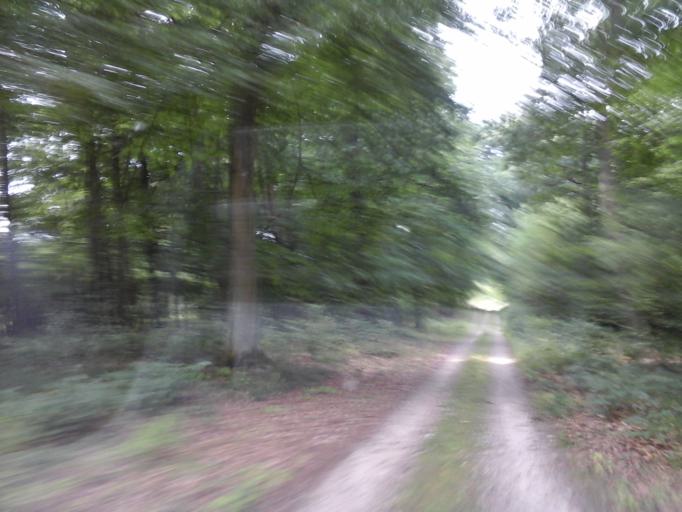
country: PL
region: West Pomeranian Voivodeship
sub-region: Powiat choszczenski
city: Bierzwnik
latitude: 53.0371
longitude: 15.5827
